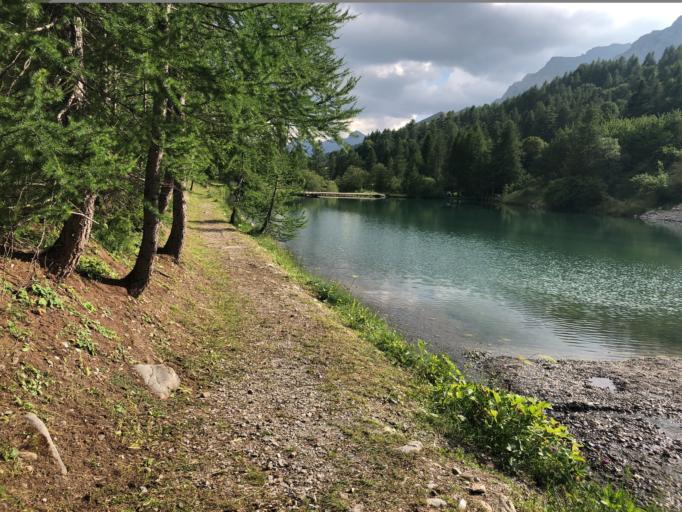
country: FR
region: Provence-Alpes-Cote d'Azur
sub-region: Departement des Alpes-de-Haute-Provence
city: Barcelonnette
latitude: 44.2374
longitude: 6.7524
